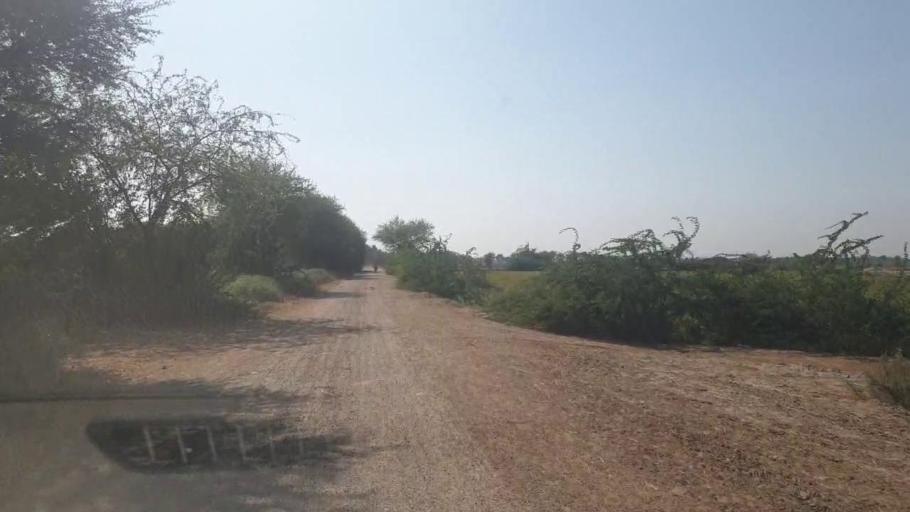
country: PK
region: Sindh
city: Badin
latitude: 24.5507
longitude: 68.8472
